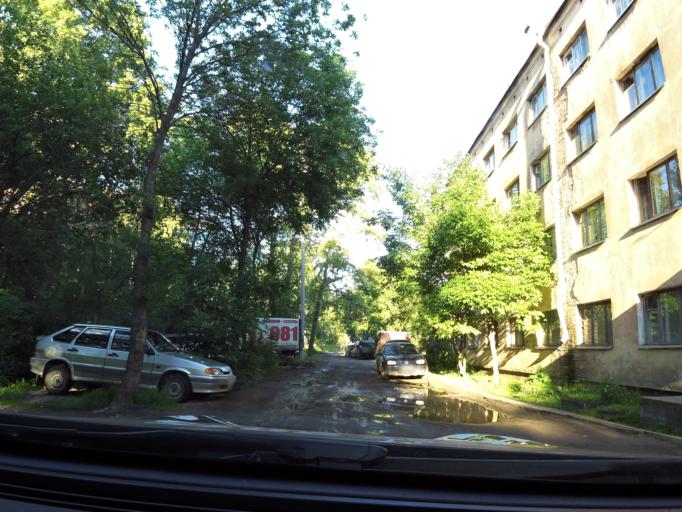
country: RU
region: Vologda
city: Vologda
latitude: 59.2191
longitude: 39.9153
